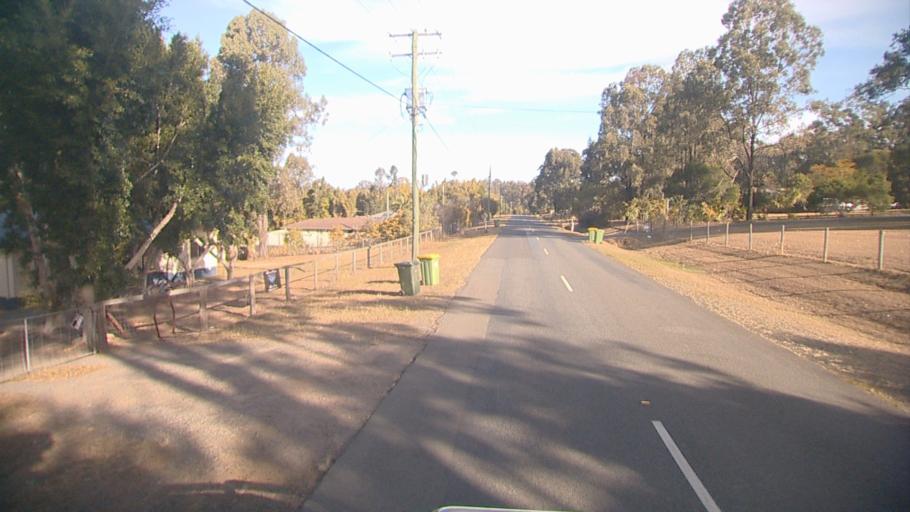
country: AU
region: Queensland
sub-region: Logan
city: Cedar Vale
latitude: -27.8765
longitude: 153.0106
